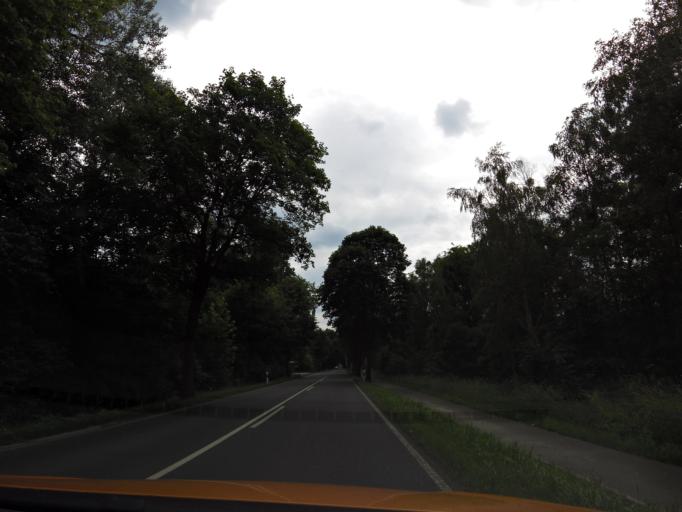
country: DE
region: Brandenburg
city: Zossen
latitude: 52.1901
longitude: 13.4622
